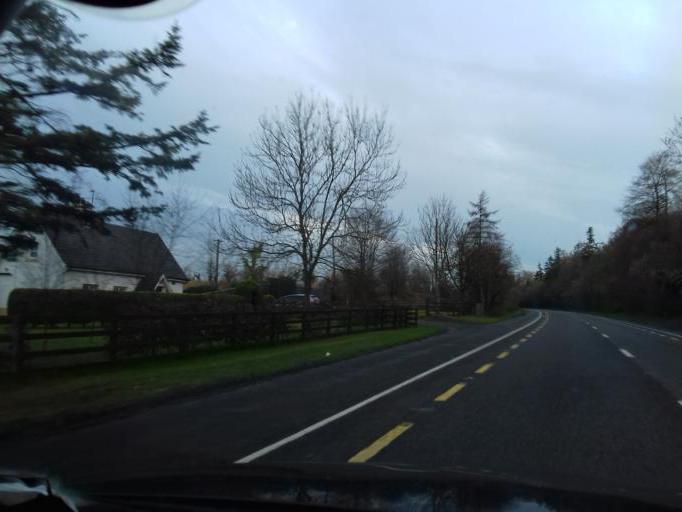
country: IE
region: Leinster
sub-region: Laois
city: Abbeyleix
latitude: 52.8713
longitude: -7.3634
